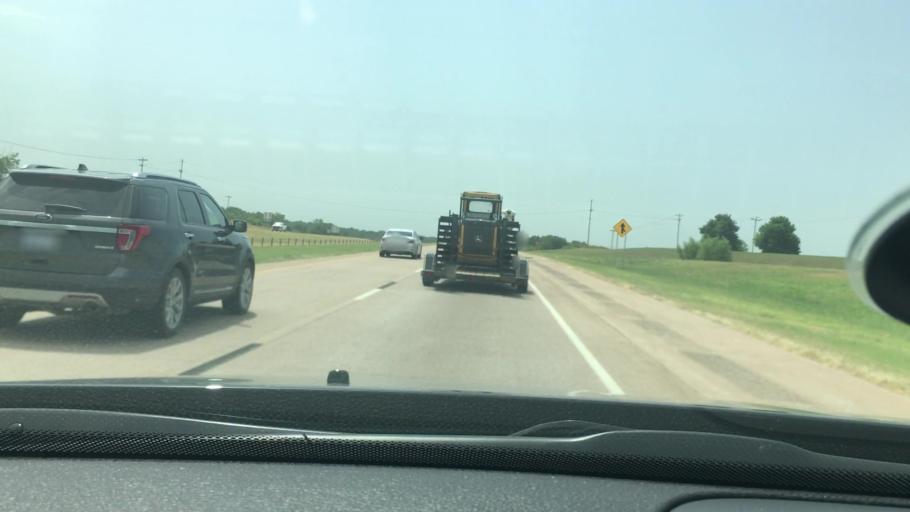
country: US
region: Oklahoma
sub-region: Garvin County
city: Pauls Valley
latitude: 34.7048
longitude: -97.2444
